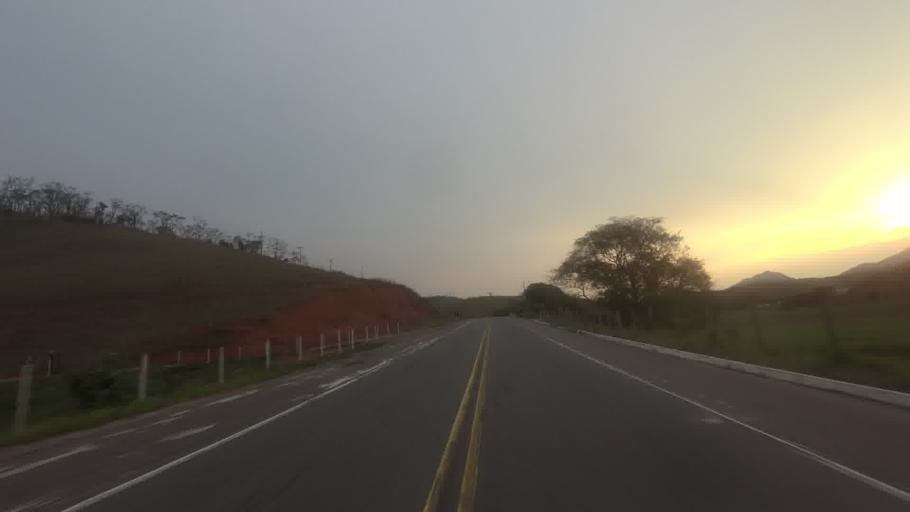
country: BR
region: Minas Gerais
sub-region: Recreio
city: Recreio
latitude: -21.7387
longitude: -42.4520
